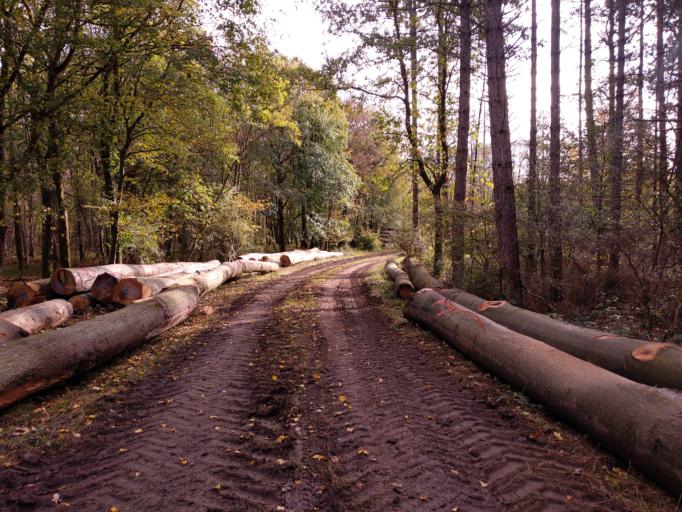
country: DE
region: North Rhine-Westphalia
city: Beverungen
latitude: 51.6883
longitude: 9.3634
